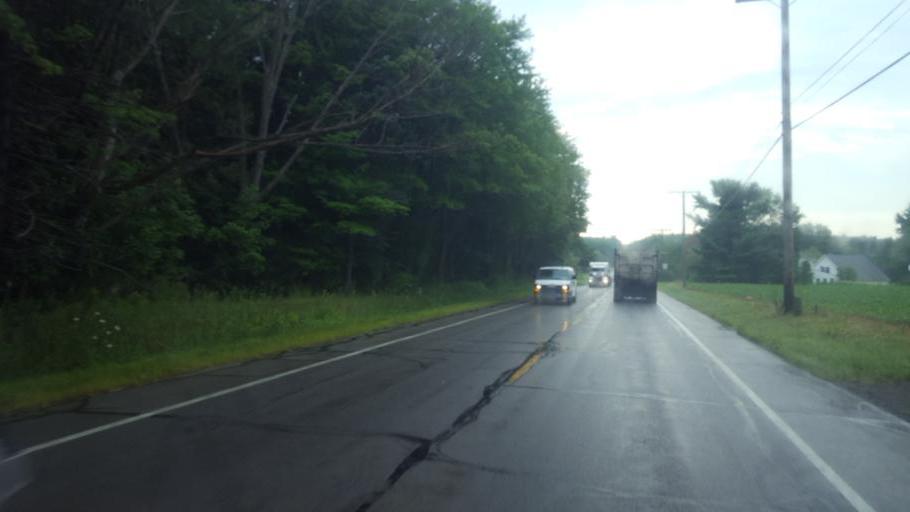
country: US
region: Ohio
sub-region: Portage County
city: Hiram
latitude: 41.3845
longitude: -81.1328
